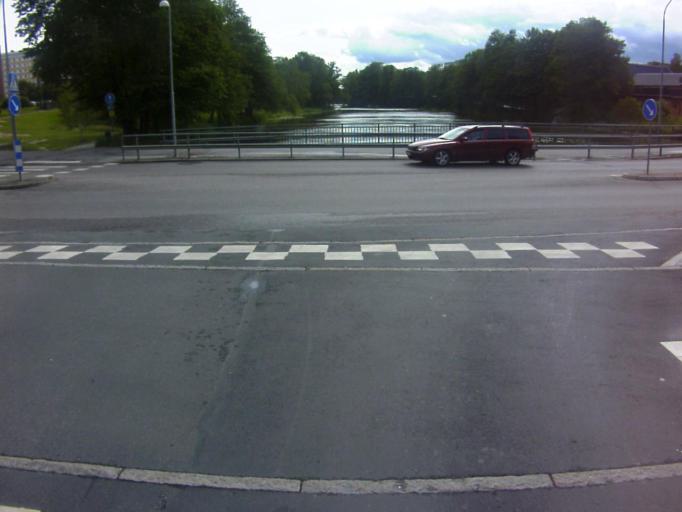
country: SE
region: Soedermanland
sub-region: Eskilstuna Kommun
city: Eskilstuna
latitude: 59.3621
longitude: 16.5124
